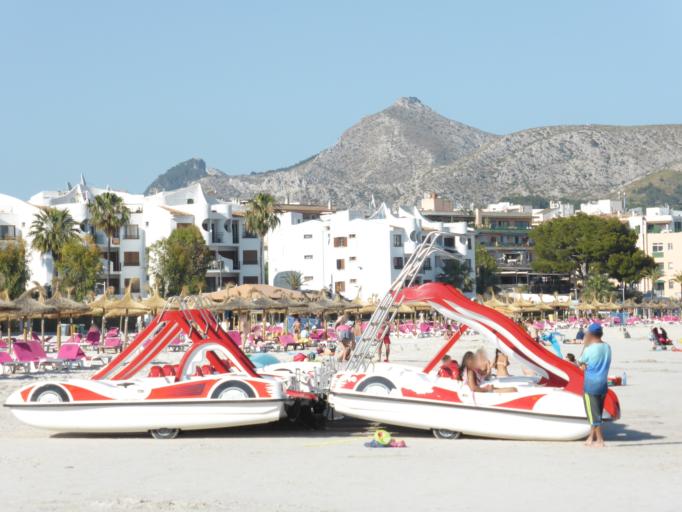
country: ES
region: Balearic Islands
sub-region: Illes Balears
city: Port d'Alcudia
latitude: 39.8398
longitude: 3.1279
